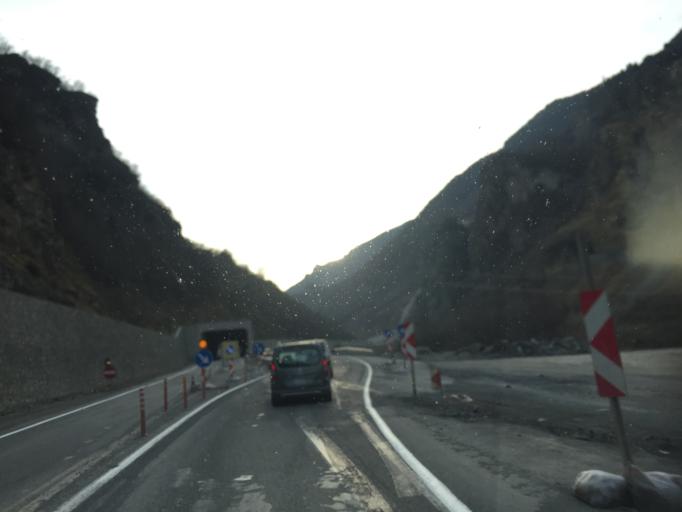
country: TR
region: Trabzon
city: Macka
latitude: 40.7385
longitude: 39.5470
